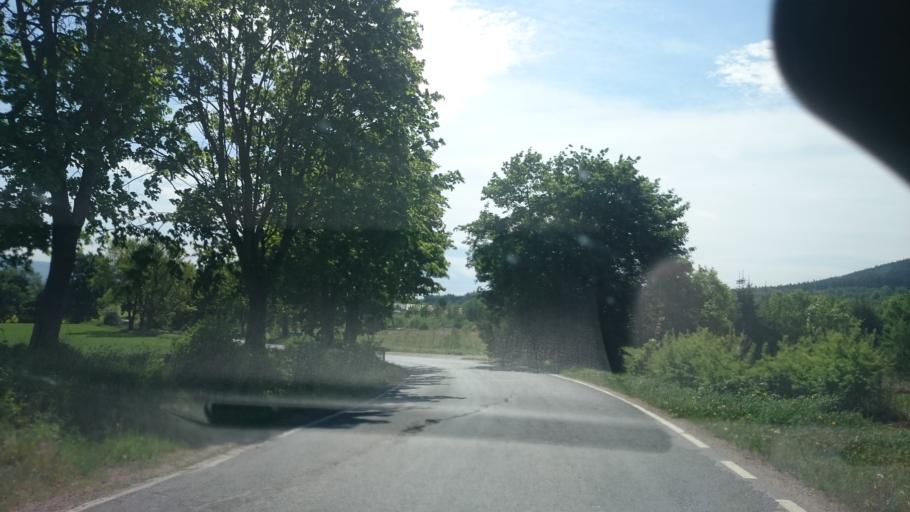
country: PL
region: Lower Silesian Voivodeship
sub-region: Powiat klodzki
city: Bystrzyca Klodzka
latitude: 50.3354
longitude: 16.5965
